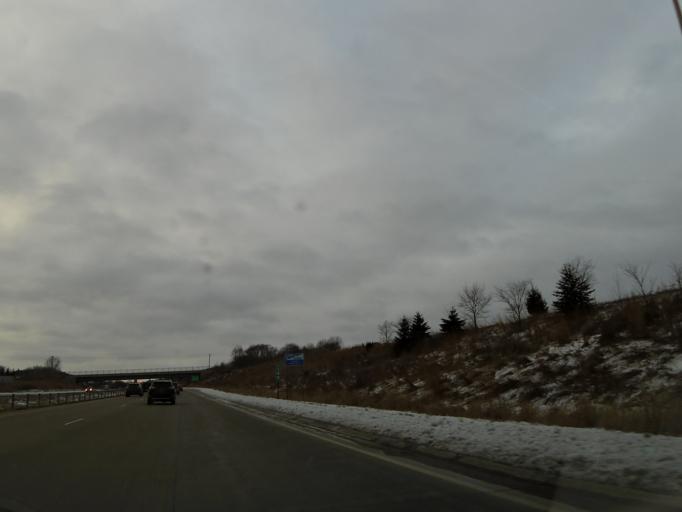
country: US
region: Minnesota
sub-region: Carver County
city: Chaska
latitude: 44.8144
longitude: -93.6095
